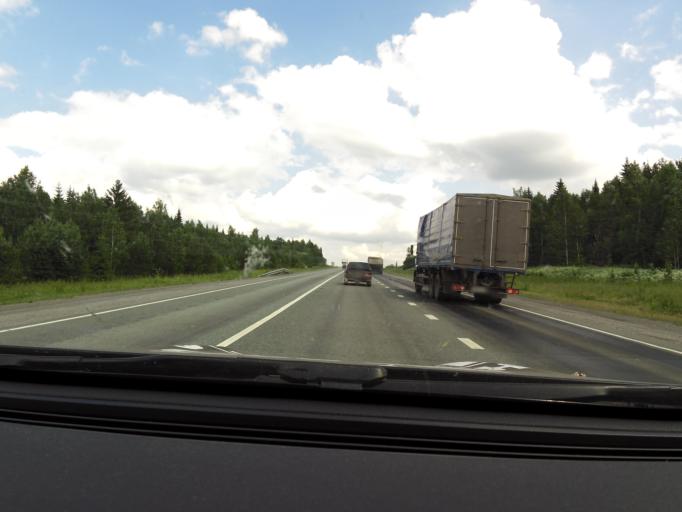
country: RU
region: Sverdlovsk
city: Bisert'
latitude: 56.7968
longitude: 58.6728
